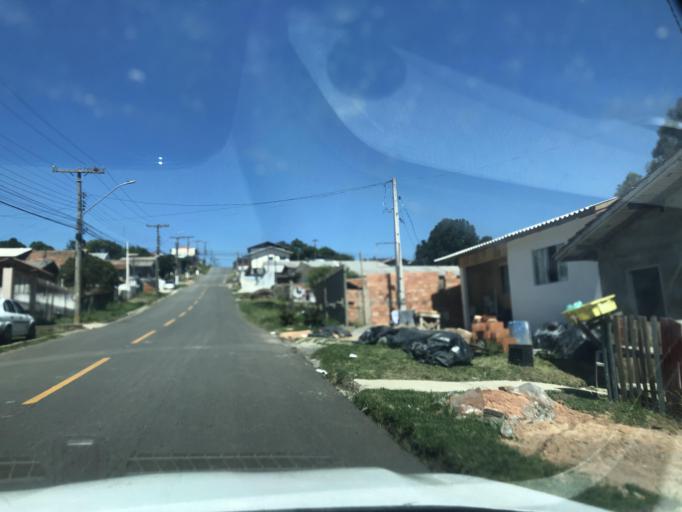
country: BR
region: Santa Catarina
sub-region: Lages
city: Lages
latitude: -27.7853
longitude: -50.3138
